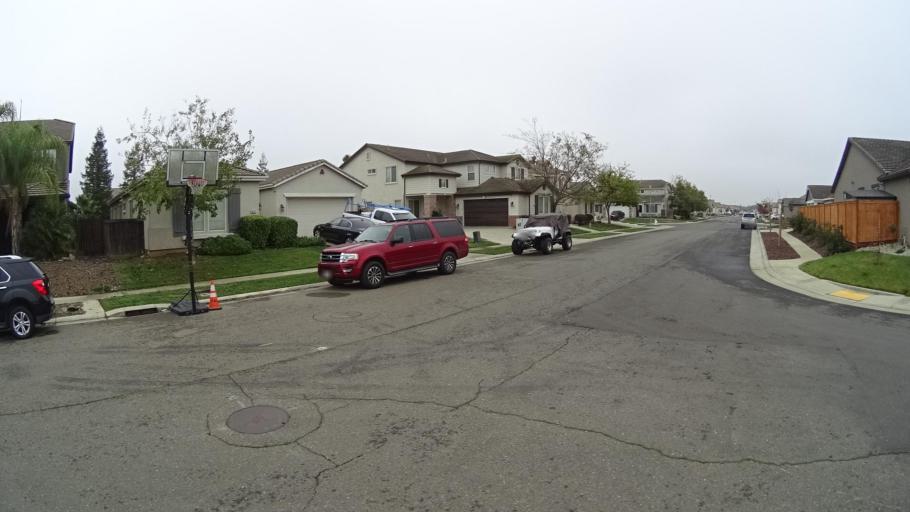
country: US
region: California
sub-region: Sacramento County
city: Elk Grove
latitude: 38.4007
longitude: -121.3482
